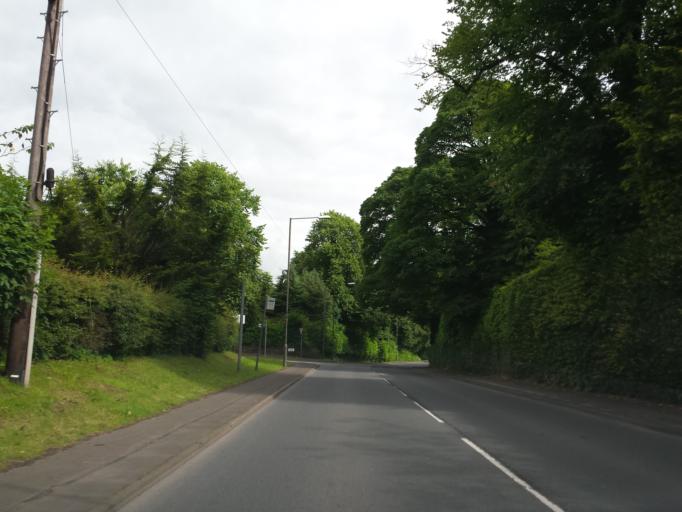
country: GB
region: Scotland
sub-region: Dumfries and Galloway
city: Moffat
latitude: 55.3269
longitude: -3.4472
